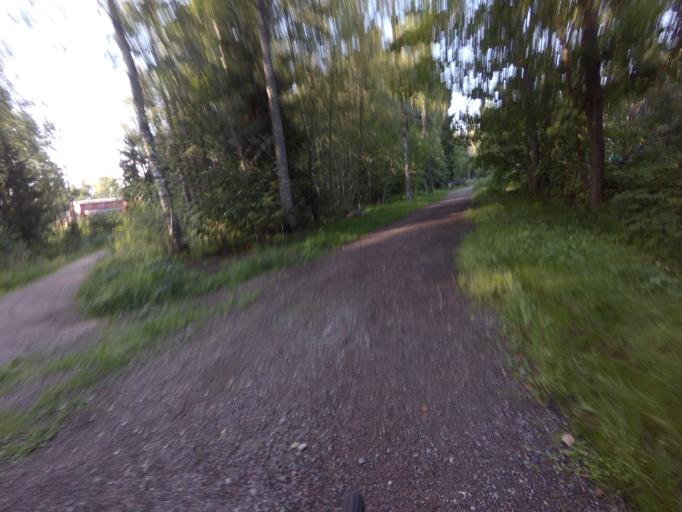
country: FI
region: Uusimaa
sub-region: Helsinki
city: Espoo
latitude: 60.1644
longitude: 24.6419
